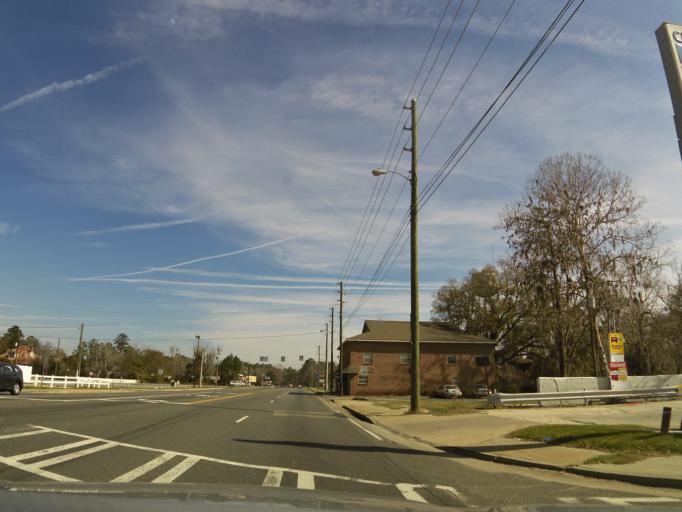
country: US
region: Georgia
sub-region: Brantley County
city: Nahunta
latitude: 31.2022
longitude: -81.9824
